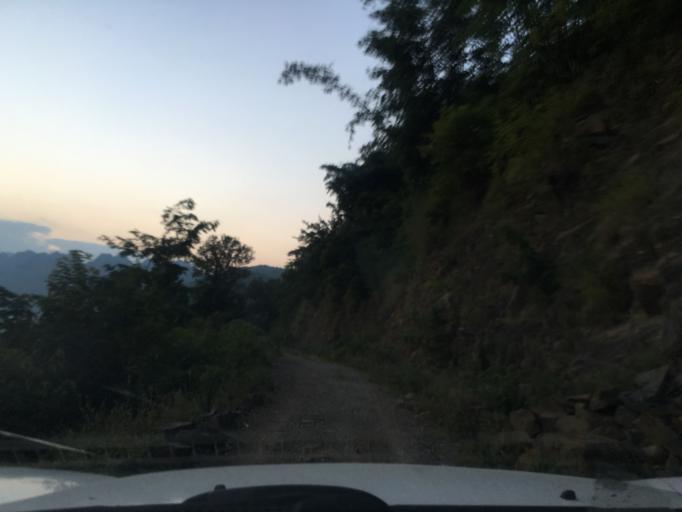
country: CN
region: Guangxi Zhuangzu Zizhiqu
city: Xinzhou
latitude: 25.3554
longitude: 105.7431
